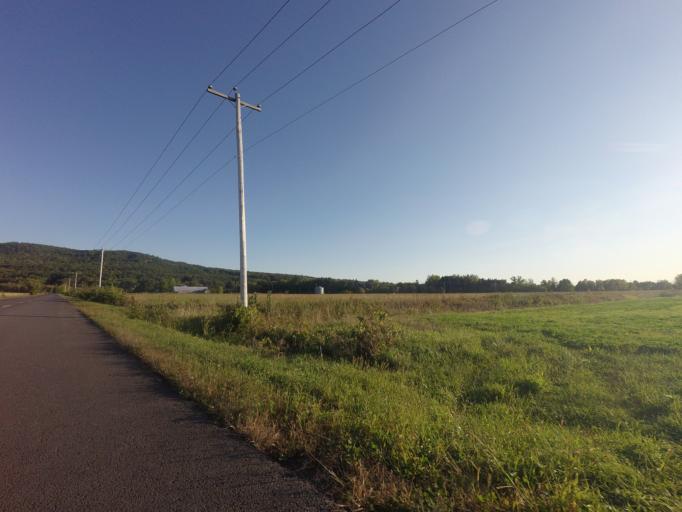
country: CA
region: Quebec
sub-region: Monteregie
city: Rigaud
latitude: 45.4756
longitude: -74.3390
